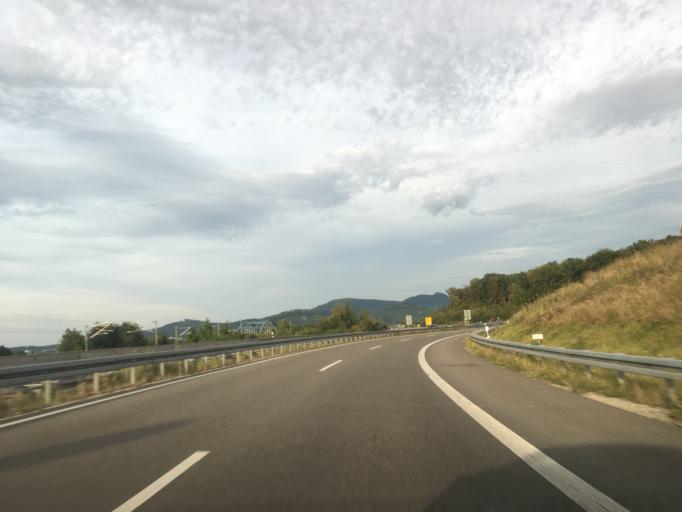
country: DE
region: Baden-Wuerttemberg
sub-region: Tuebingen Region
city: Metzingen
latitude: 48.5274
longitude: 9.2594
